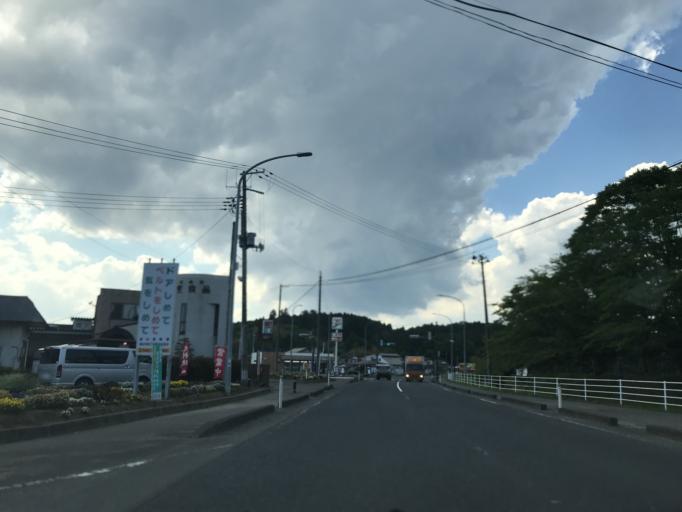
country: JP
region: Miyagi
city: Wakuya
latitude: 38.5441
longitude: 141.1441
